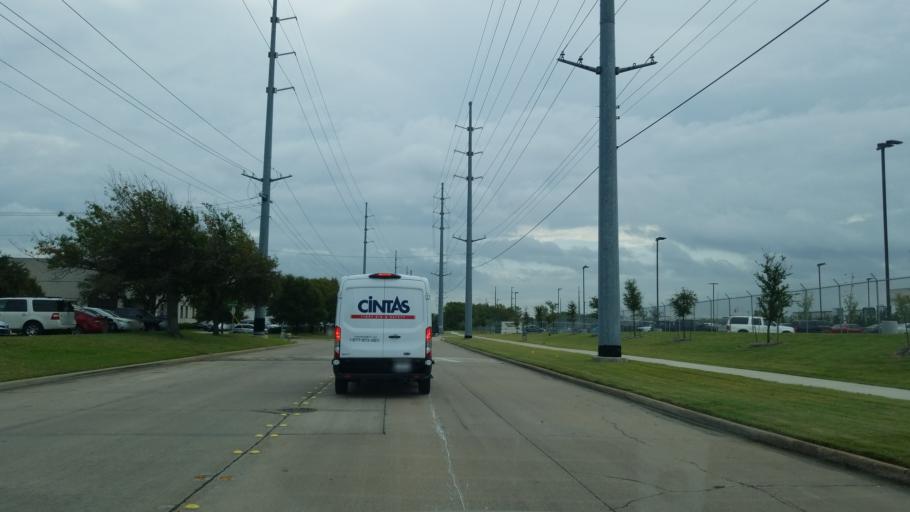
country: US
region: Texas
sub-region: Dallas County
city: Garland
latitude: 32.9010
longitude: -96.6720
